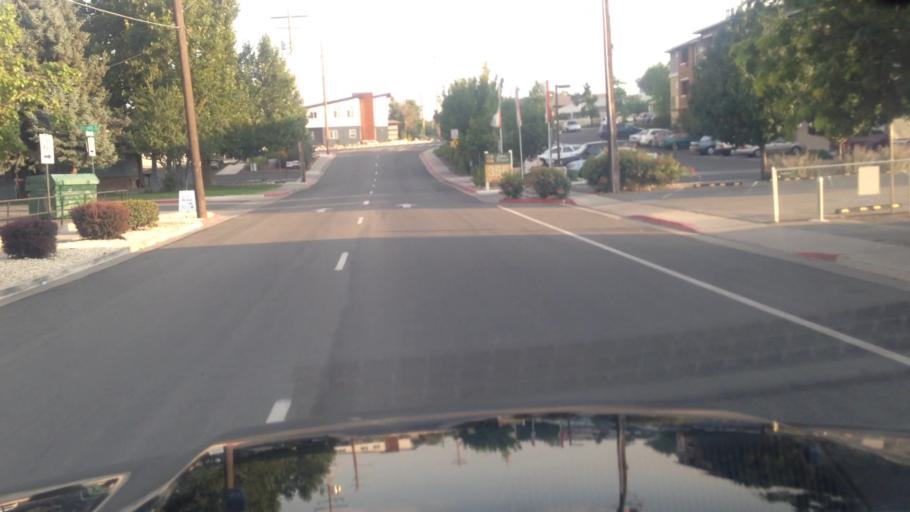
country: US
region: Nevada
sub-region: Washoe County
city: Reno
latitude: 39.5236
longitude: -119.7983
